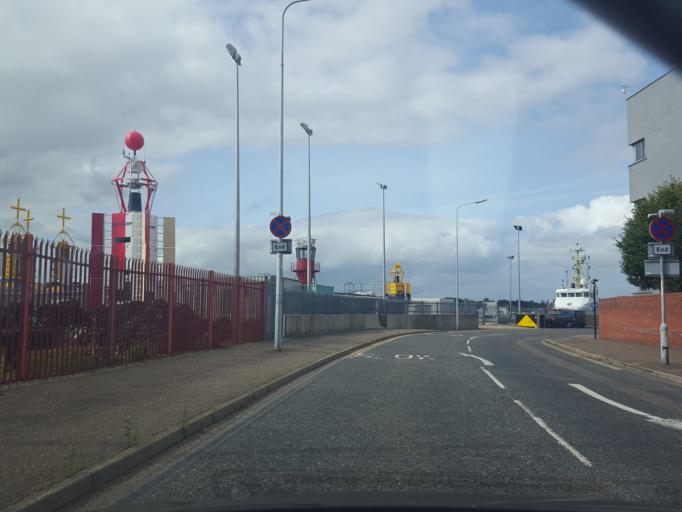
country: GB
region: England
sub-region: Essex
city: Harwich
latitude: 51.9464
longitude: 1.2850
